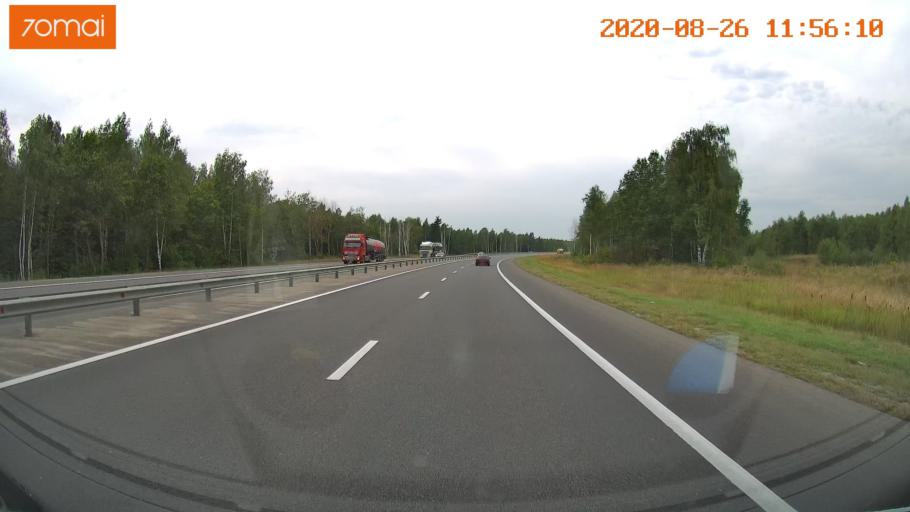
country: RU
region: Rjazan
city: Kiritsy
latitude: 54.2641
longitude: 40.3838
